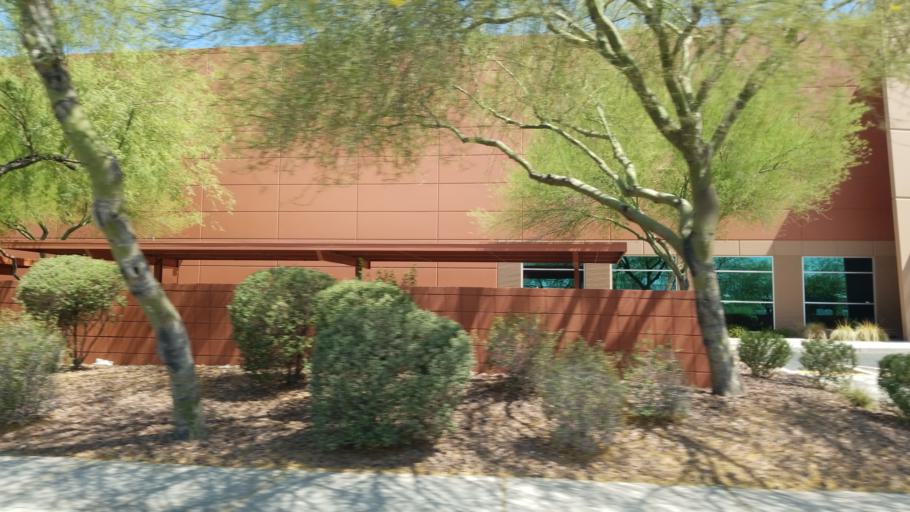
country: US
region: Arizona
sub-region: Maricopa County
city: Laveen
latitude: 33.4312
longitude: -112.1541
